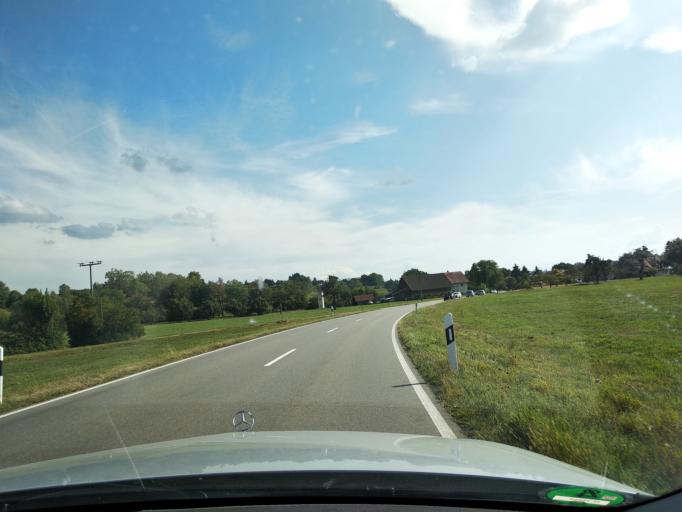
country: DE
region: Baden-Wuerttemberg
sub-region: Tuebingen Region
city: Amtzell
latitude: 47.6801
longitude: 9.7643
